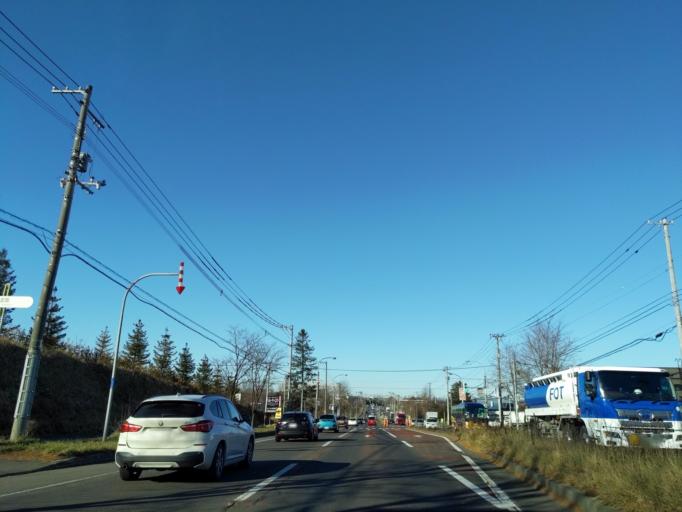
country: JP
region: Hokkaido
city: Kitahiroshima
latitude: 42.9470
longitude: 141.5001
